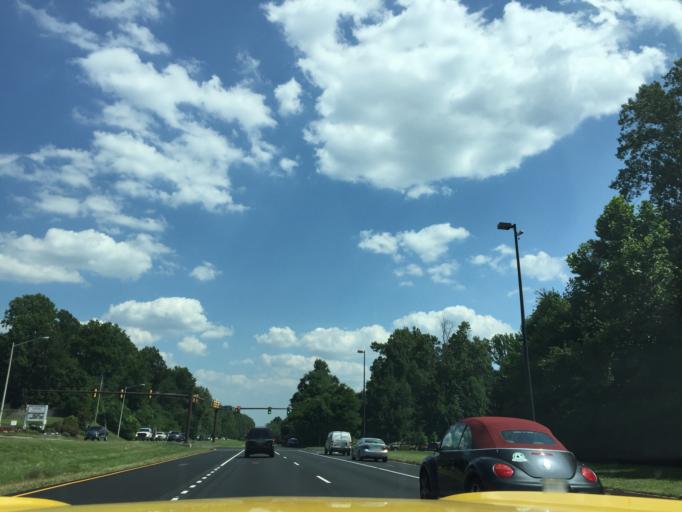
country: US
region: Virginia
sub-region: Fairfax County
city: Dranesville
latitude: 38.9951
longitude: -77.3373
